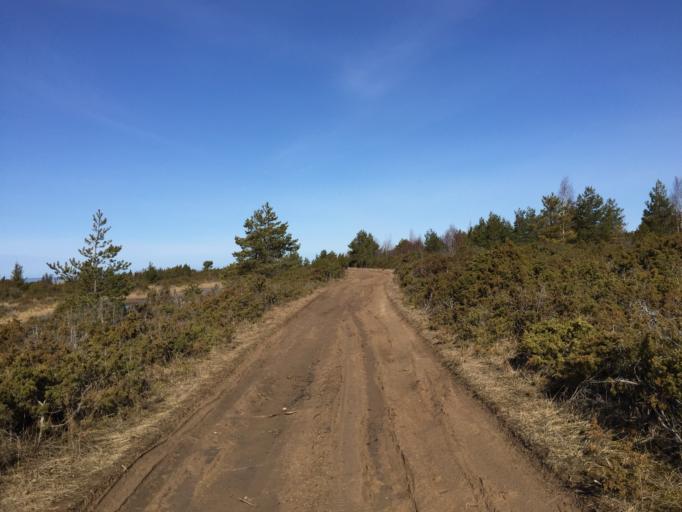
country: EE
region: Laeaene
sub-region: Haapsalu linn
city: Haapsalu
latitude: 58.6485
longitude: 23.5096
